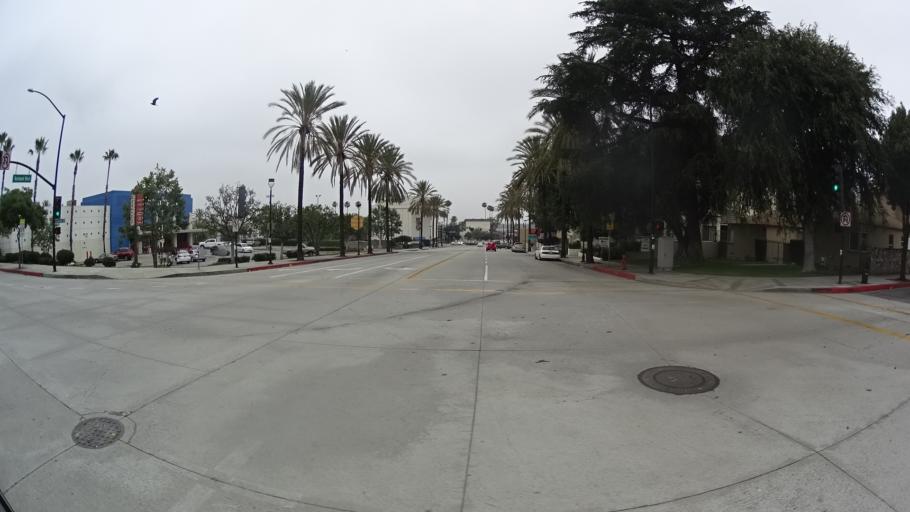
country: US
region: California
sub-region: Los Angeles County
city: Burbank
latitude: 34.1874
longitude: -118.3149
